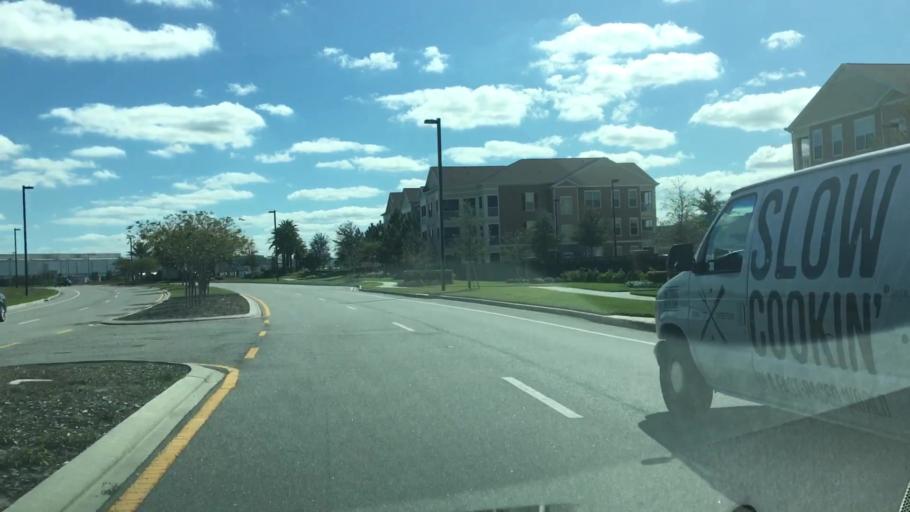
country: US
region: Florida
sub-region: Orange County
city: Conway
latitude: 28.4582
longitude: -81.2897
